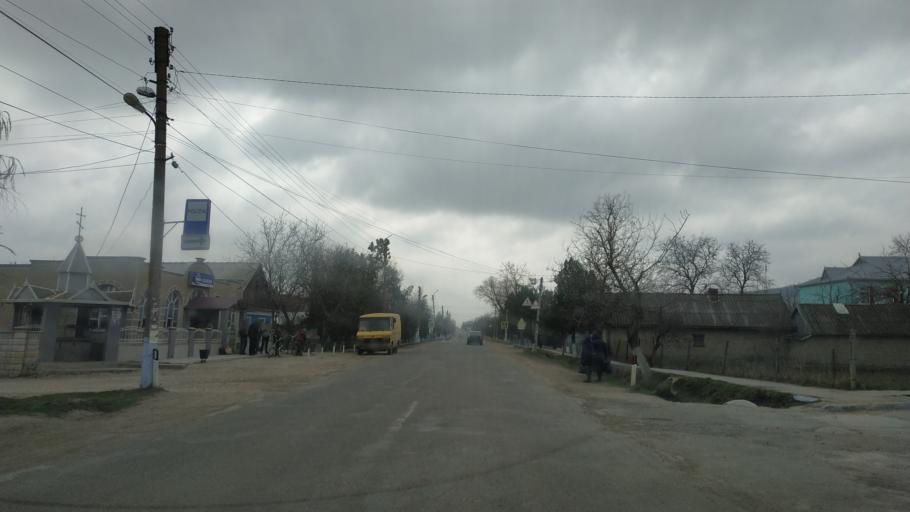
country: MD
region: Basarabeasca
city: Basarabeasca
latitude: 46.3638
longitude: 28.9338
